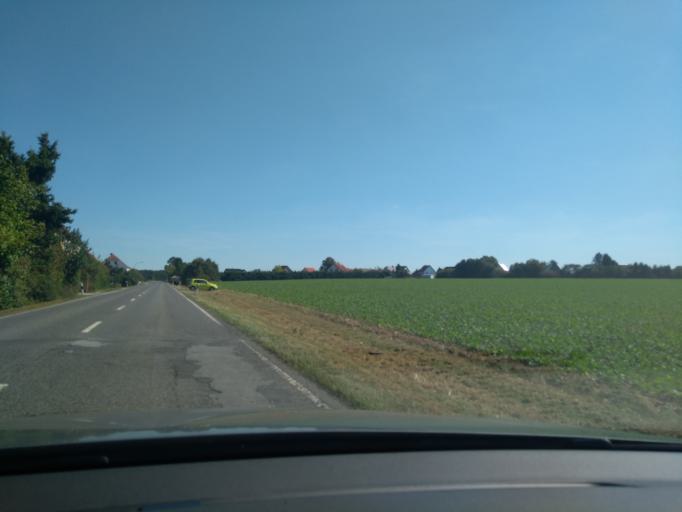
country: DE
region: Saxony
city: Goda
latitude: 51.1914
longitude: 14.3488
